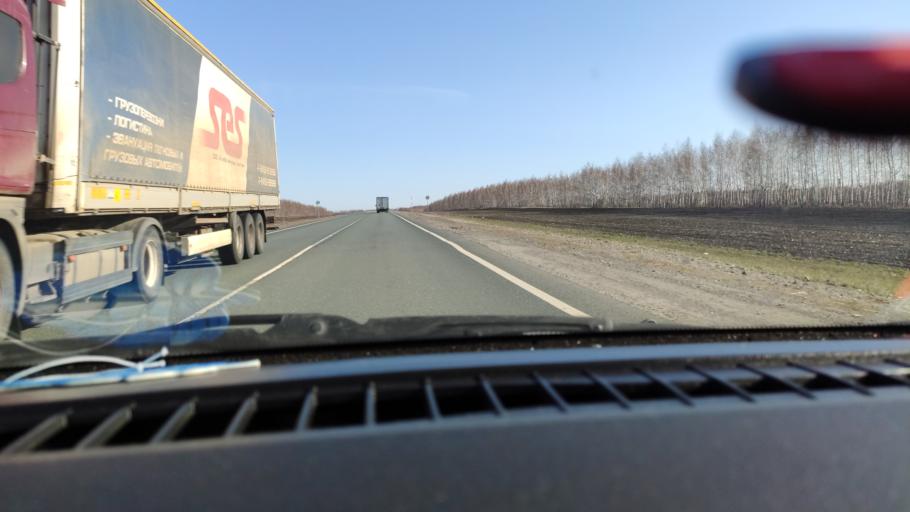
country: RU
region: Samara
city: Syzran'
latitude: 52.9069
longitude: 48.2985
